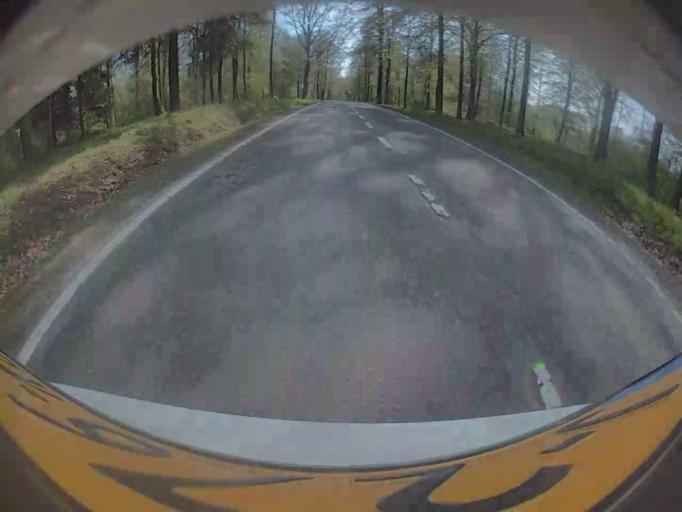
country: BE
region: Wallonia
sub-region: Province de Namur
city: Hamois
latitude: 50.2982
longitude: 5.2109
